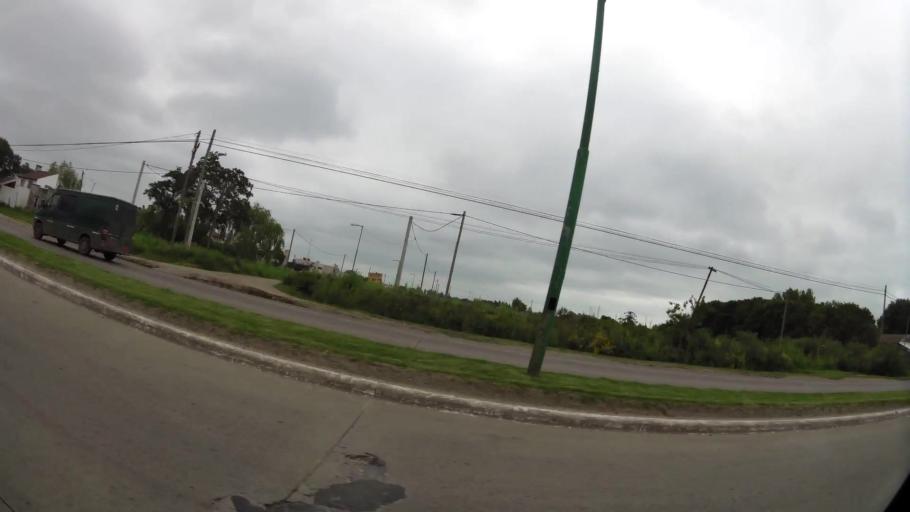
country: AR
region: Buenos Aires
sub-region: Partido de La Plata
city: La Plata
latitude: -35.0091
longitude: -58.0632
